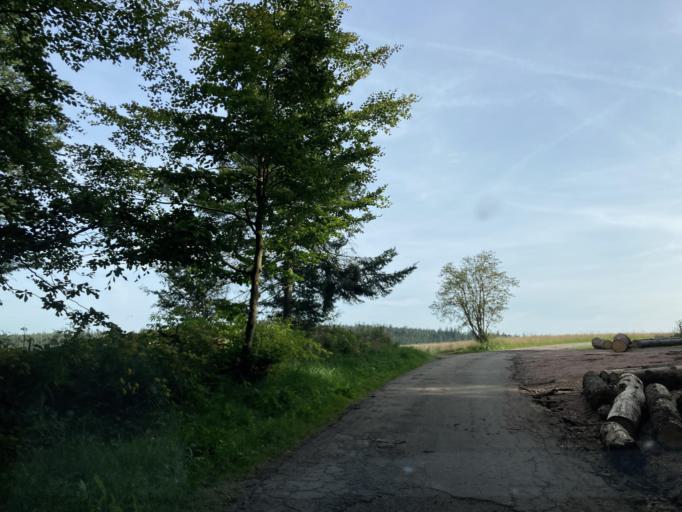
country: DE
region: Baden-Wuerttemberg
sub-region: Freiburg Region
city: Furtwangen im Schwarzwald
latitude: 47.9936
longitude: 8.1972
